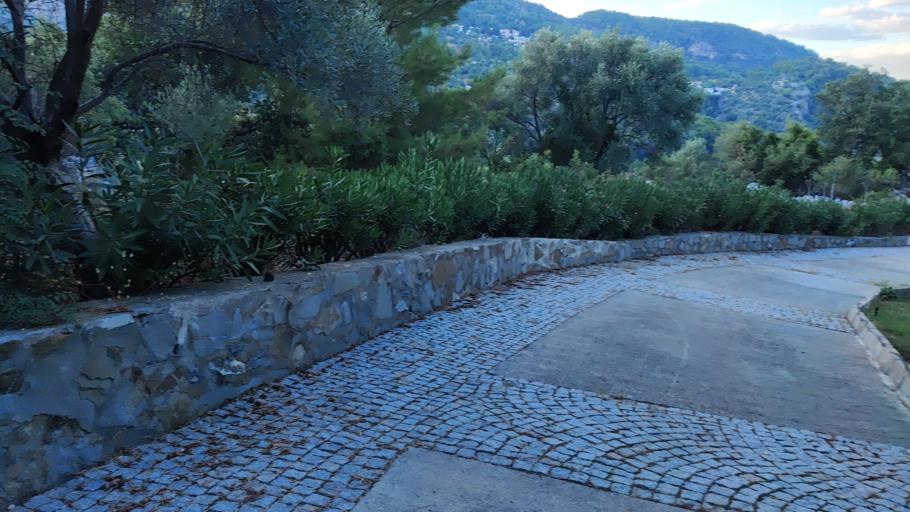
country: TR
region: Mugla
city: Sarigerme
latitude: 36.7062
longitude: 28.6930
